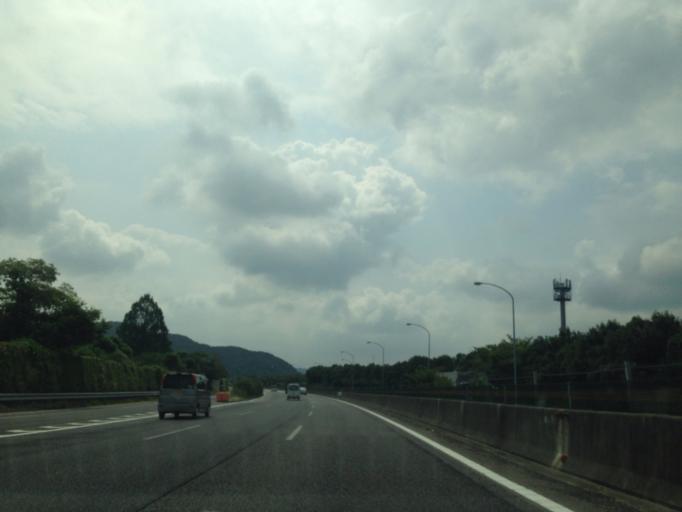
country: JP
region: Aichi
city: Gamagori
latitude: 34.8958
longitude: 137.2579
